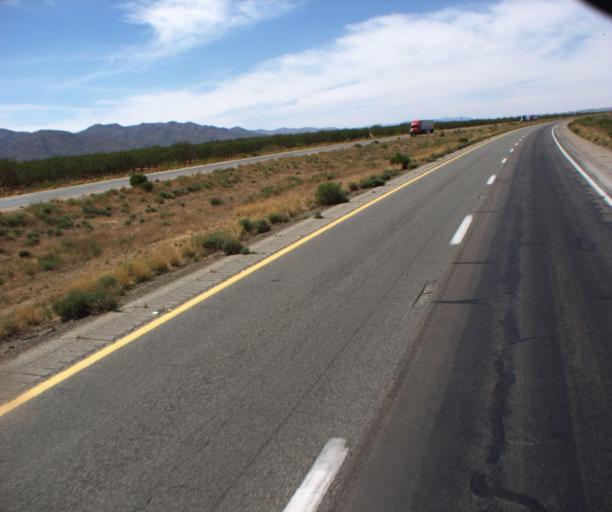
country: US
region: Arizona
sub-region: Cochise County
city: Willcox
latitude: 32.3183
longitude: -109.4917
